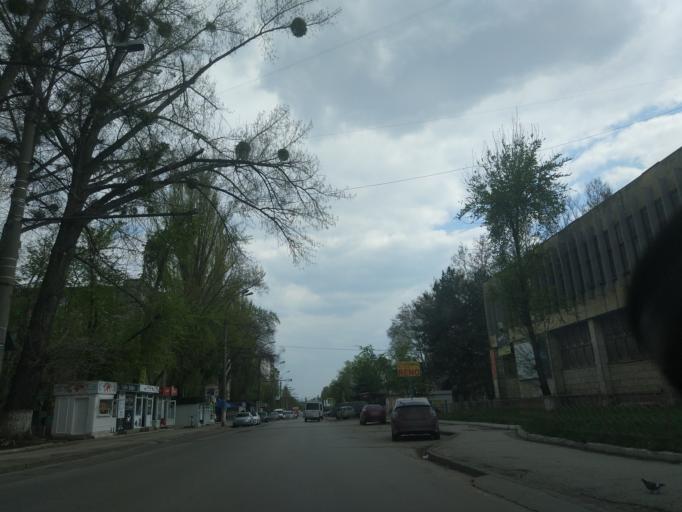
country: MD
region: Chisinau
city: Chisinau
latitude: 46.9847
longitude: 28.8761
